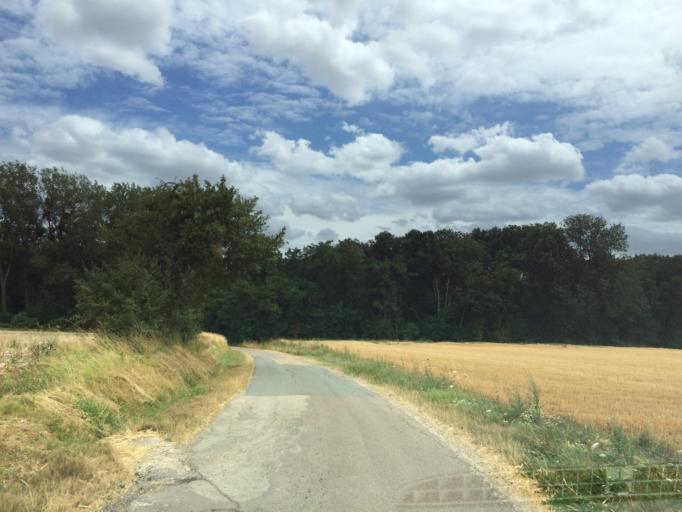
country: FR
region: Bourgogne
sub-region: Departement de l'Yonne
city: Fleury-la-Vallee
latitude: 47.8456
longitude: 3.4097
